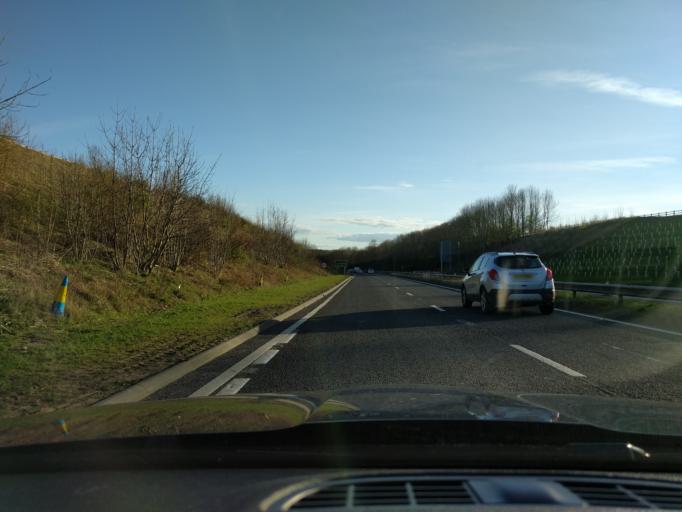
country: GB
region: England
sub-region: Northumberland
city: Morpeth
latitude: 55.1720
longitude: -1.7221
